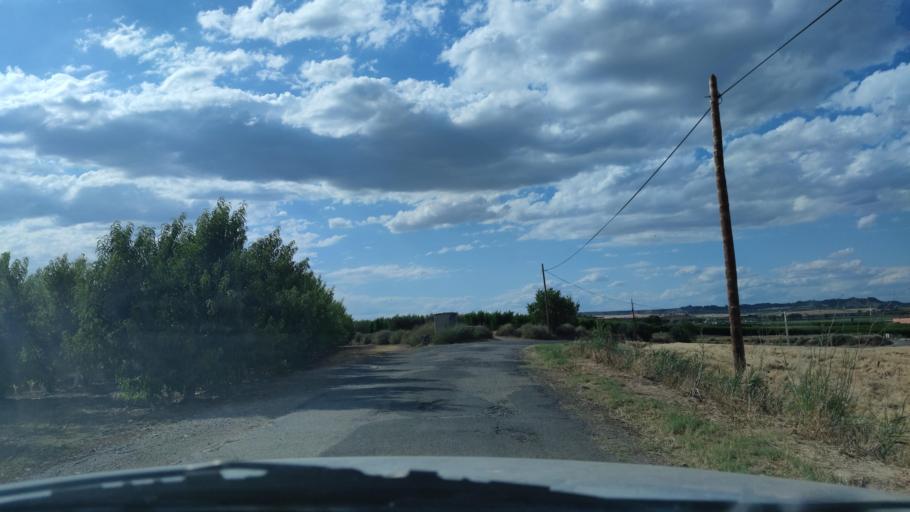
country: ES
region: Catalonia
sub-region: Provincia de Lleida
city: Alcarras
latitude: 41.5909
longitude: 0.5318
